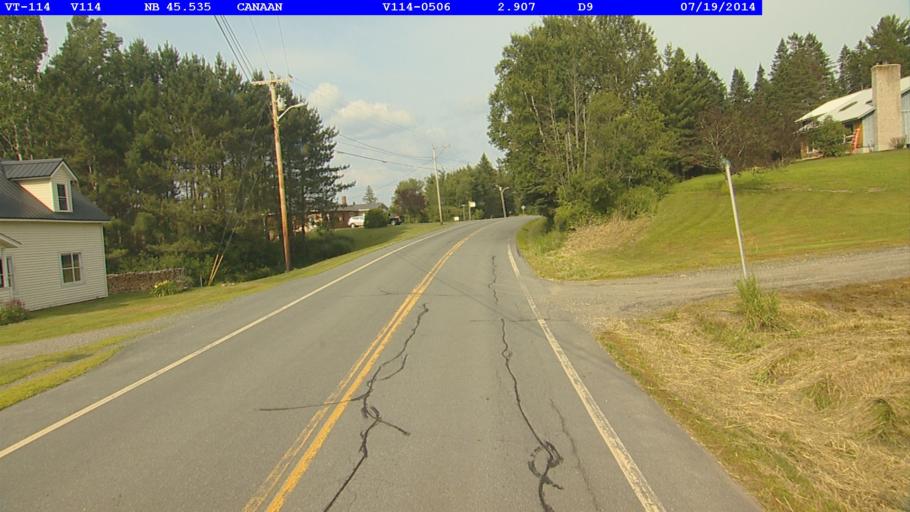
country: US
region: New Hampshire
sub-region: Coos County
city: Colebrook
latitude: 45.0078
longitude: -71.6352
